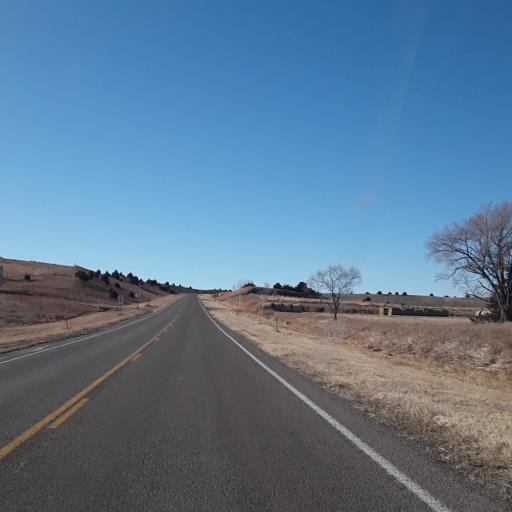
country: US
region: Nebraska
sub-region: Frontier County
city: Stockville
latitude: 40.6324
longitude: -100.5753
